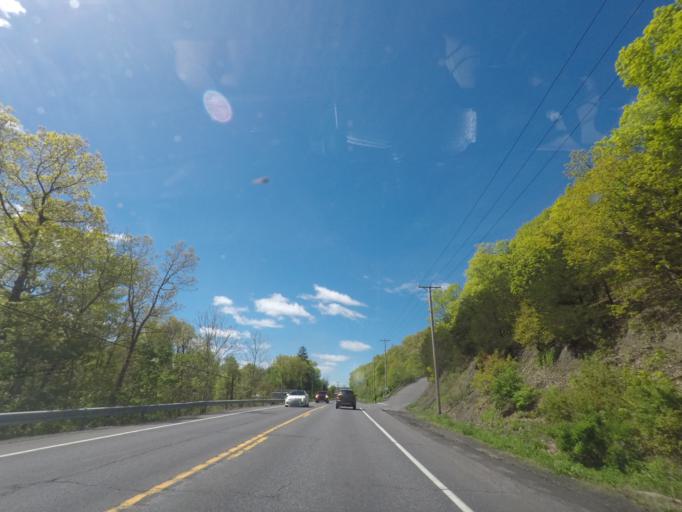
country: US
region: New York
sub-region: Ulster County
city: Lake Katrine
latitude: 42.0135
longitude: -73.9798
